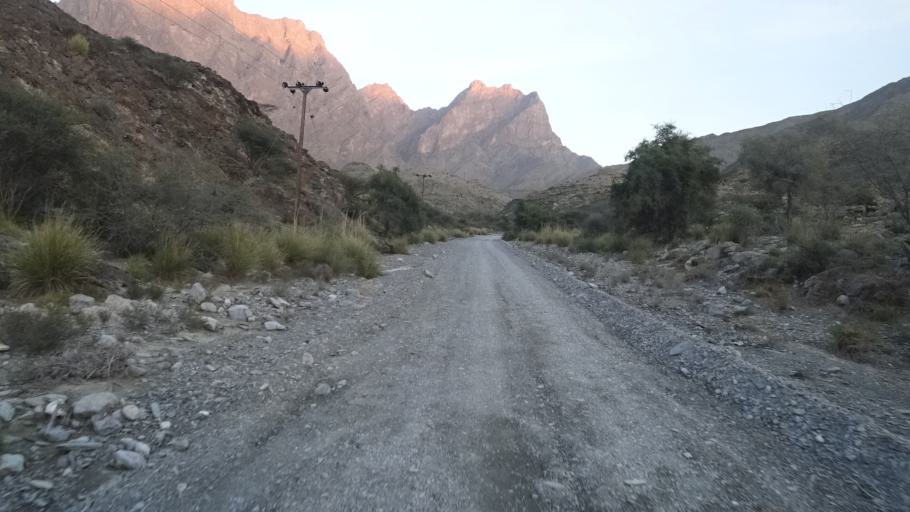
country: OM
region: Al Batinah
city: Bayt al `Awabi
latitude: 23.2403
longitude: 57.4386
